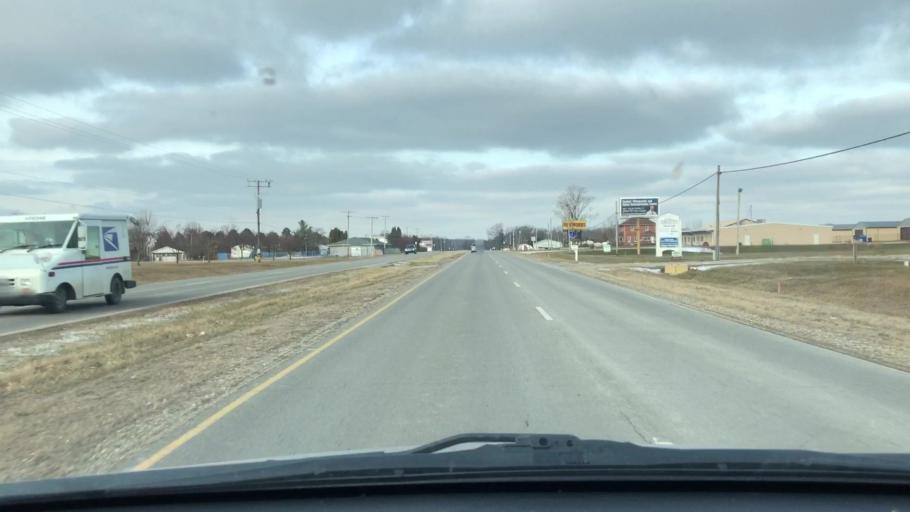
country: US
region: Indiana
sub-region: Steuben County
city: Angola
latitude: 41.6736
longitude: -85.0287
